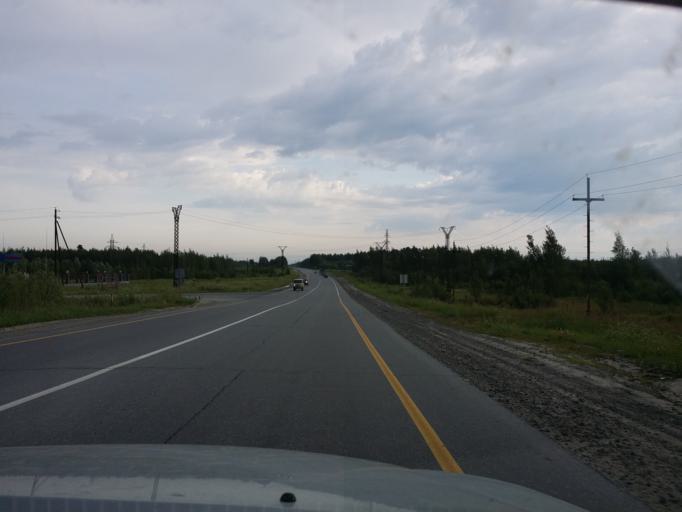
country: RU
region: Khanty-Mansiyskiy Avtonomnyy Okrug
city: Megion
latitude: 61.0569
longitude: 76.1138
